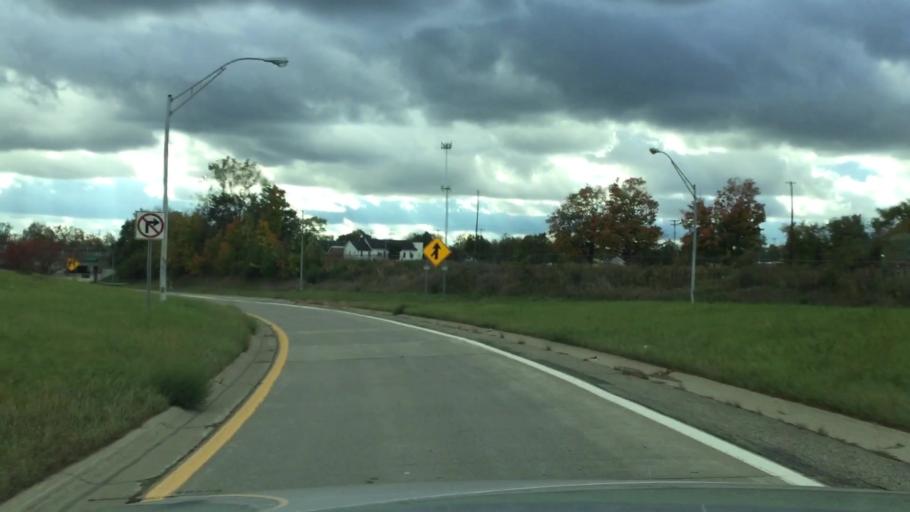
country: US
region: Michigan
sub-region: Genesee County
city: Flint
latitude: 43.0088
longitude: -83.6799
